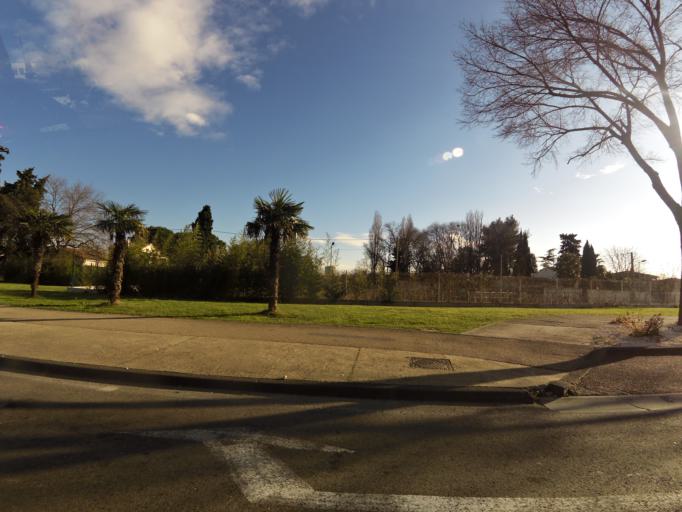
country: FR
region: Languedoc-Roussillon
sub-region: Departement du Gard
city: Nimes
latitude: 43.8308
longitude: 4.3808
